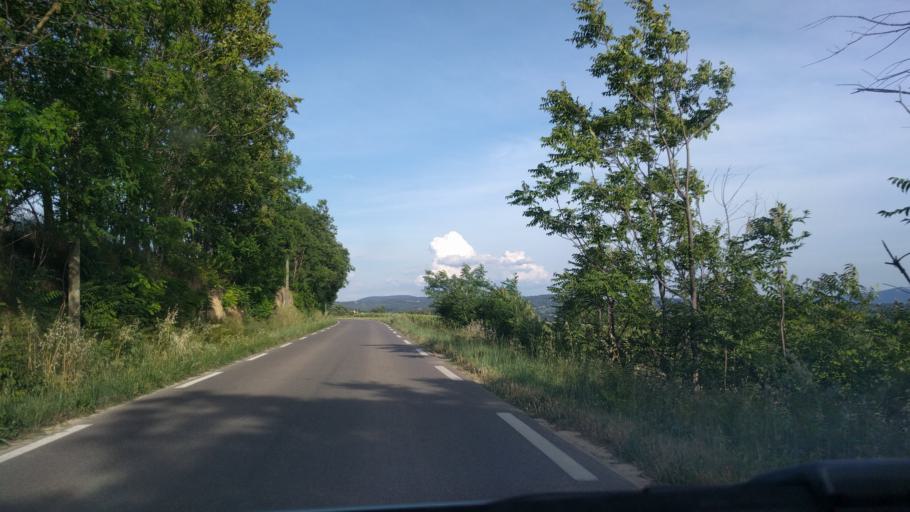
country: FR
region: Provence-Alpes-Cote d'Azur
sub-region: Departement du Vaucluse
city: Pertuis
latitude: 43.7343
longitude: 5.5210
